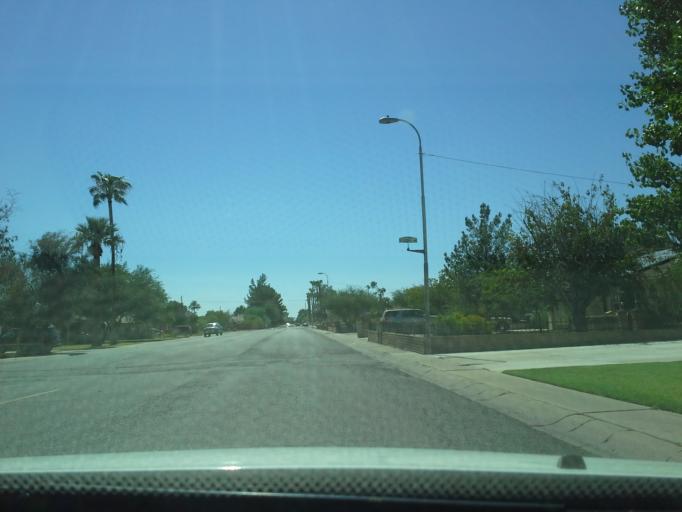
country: US
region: Arizona
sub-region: Maricopa County
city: Phoenix
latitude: 33.5169
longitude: -112.1021
